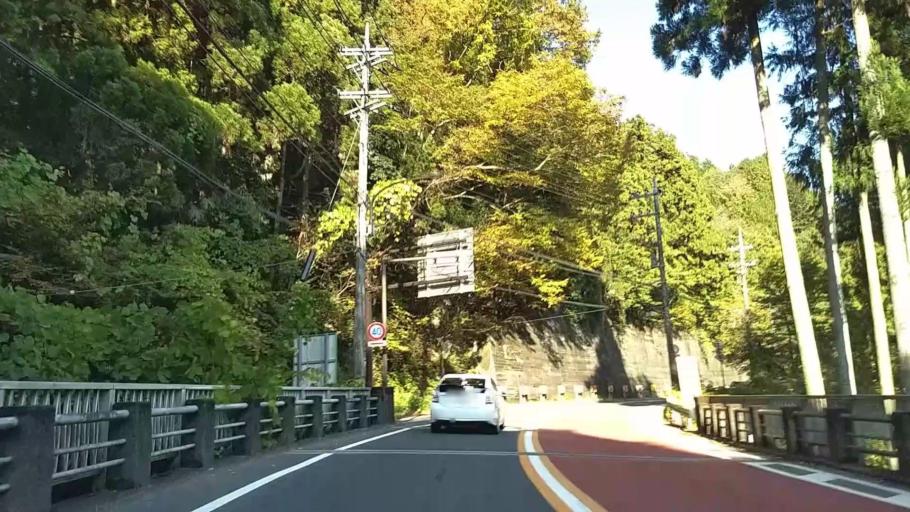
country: JP
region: Tokyo
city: Ome
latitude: 35.8145
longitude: 139.1350
